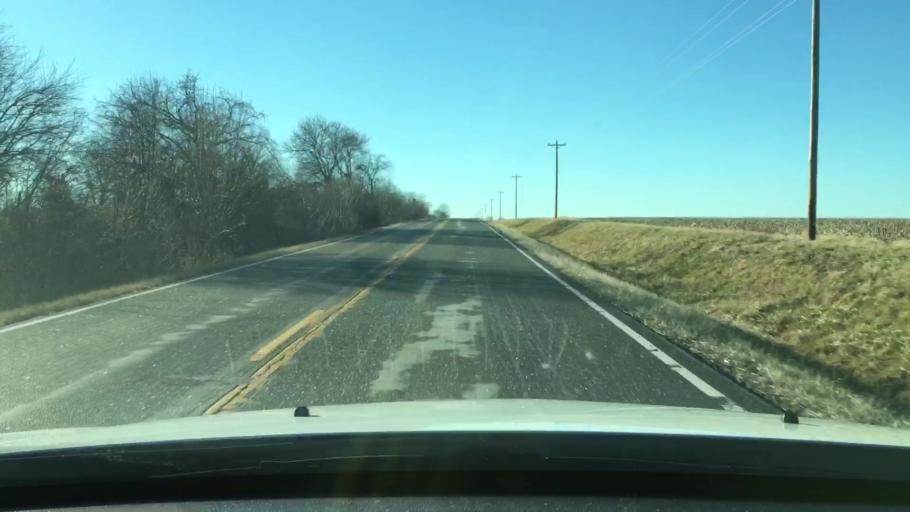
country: US
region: Missouri
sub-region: Audrain County
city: Mexico
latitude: 39.2816
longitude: -91.7222
